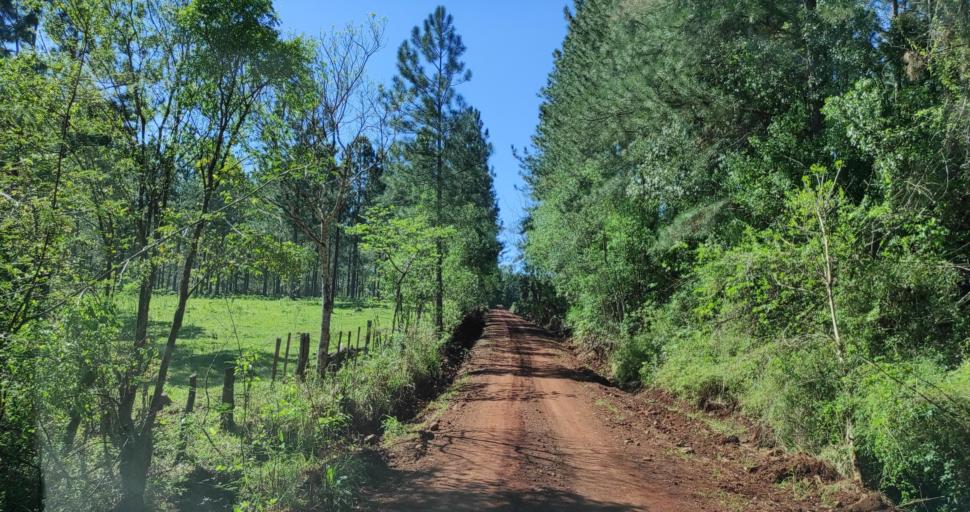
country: AR
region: Misiones
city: Ruiz de Montoya
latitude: -26.9488
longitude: -55.0030
